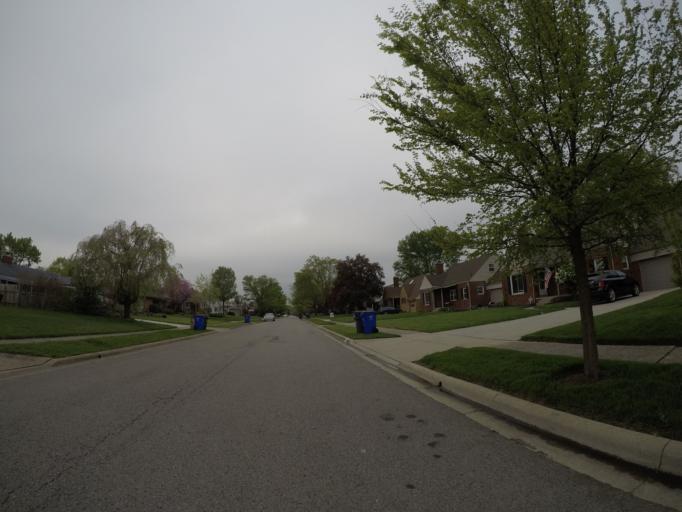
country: US
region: Ohio
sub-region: Franklin County
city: Upper Arlington
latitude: 40.0183
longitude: -83.0662
